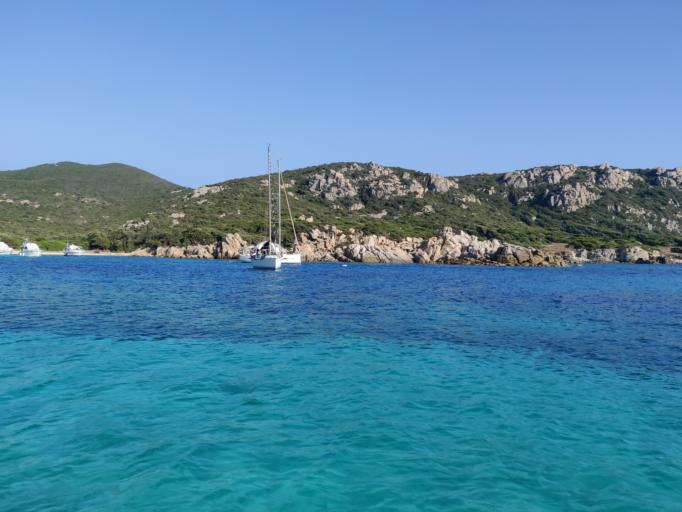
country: FR
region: Corsica
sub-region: Departement de la Corse-du-Sud
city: Propriano
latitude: 41.5754
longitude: 8.8011
